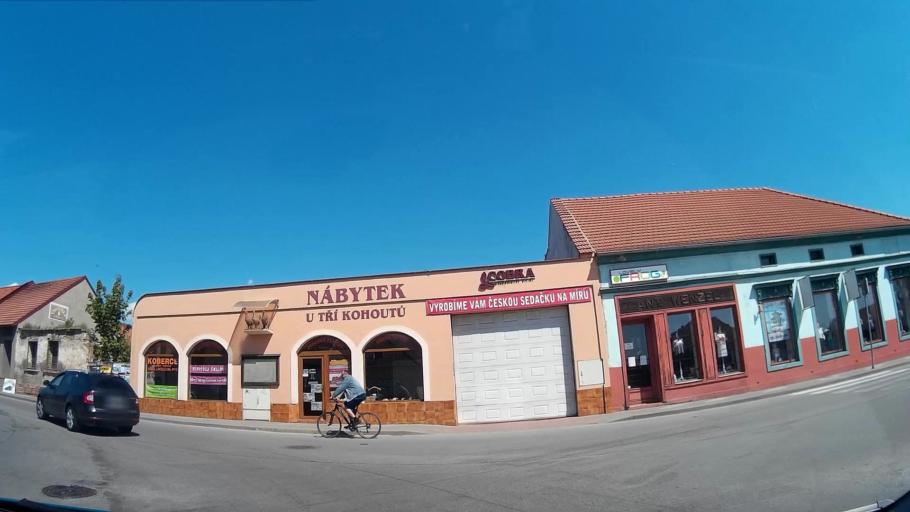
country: CZ
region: South Moravian
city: Ivancice
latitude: 49.1031
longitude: 16.3751
